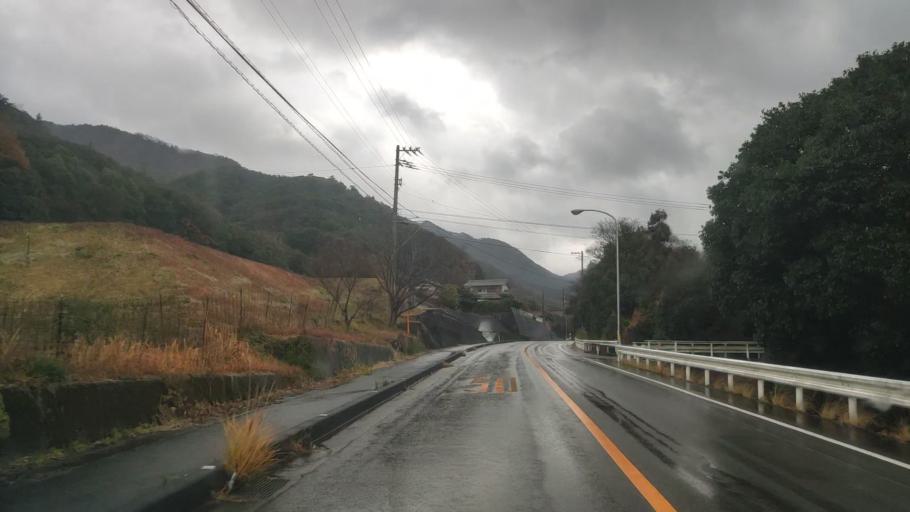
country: JP
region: Tokushima
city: Kamojimacho-jogejima
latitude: 34.1970
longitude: 134.3320
